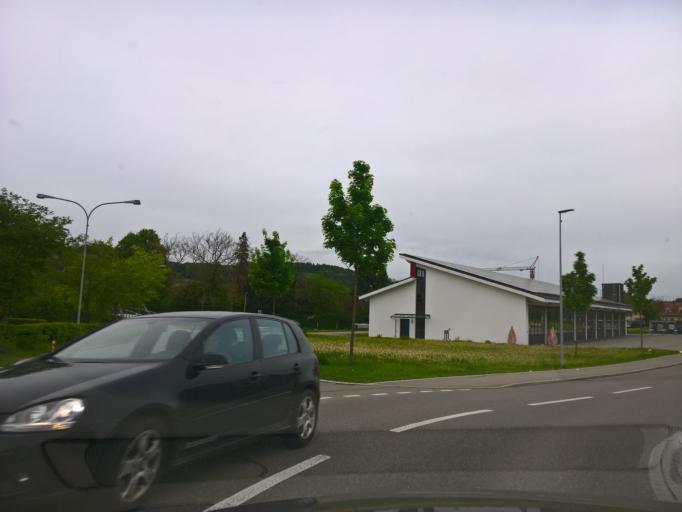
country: CH
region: Zurich
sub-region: Bezirk Winterthur
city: Pfungen
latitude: 47.5171
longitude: 8.6430
